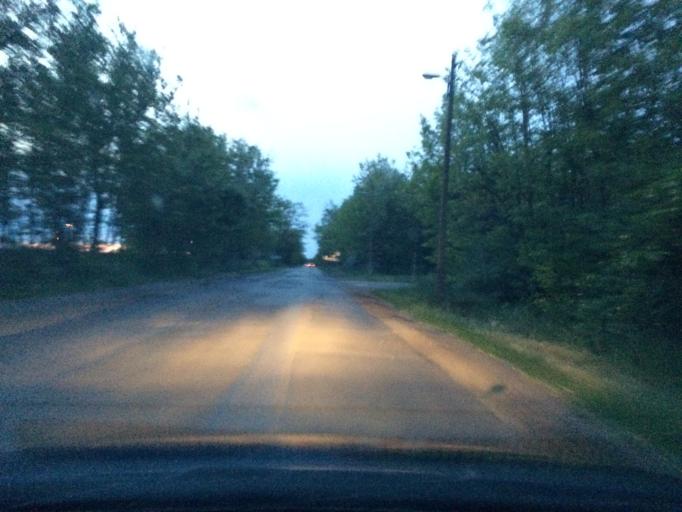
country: HU
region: Hajdu-Bihar
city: Hajdunanas
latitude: 47.9088
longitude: 21.4018
